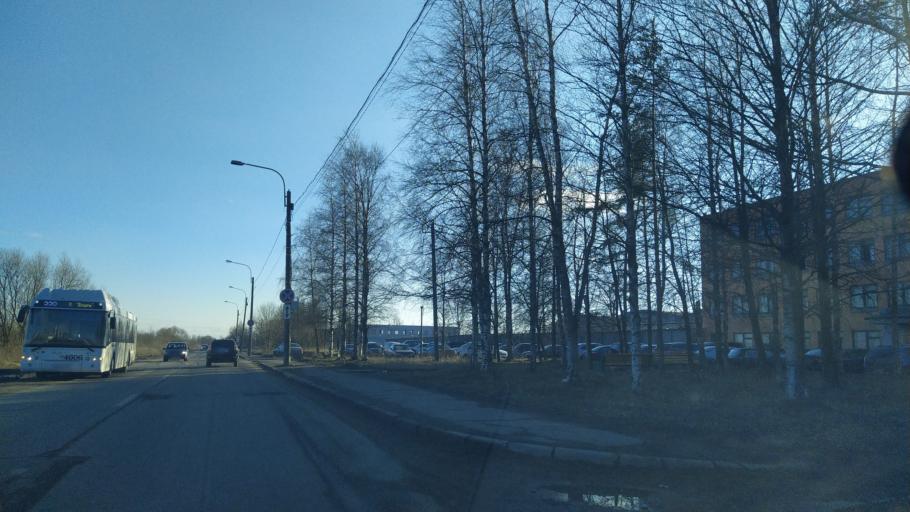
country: RU
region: St.-Petersburg
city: Pushkin
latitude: 59.6970
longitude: 30.3952
